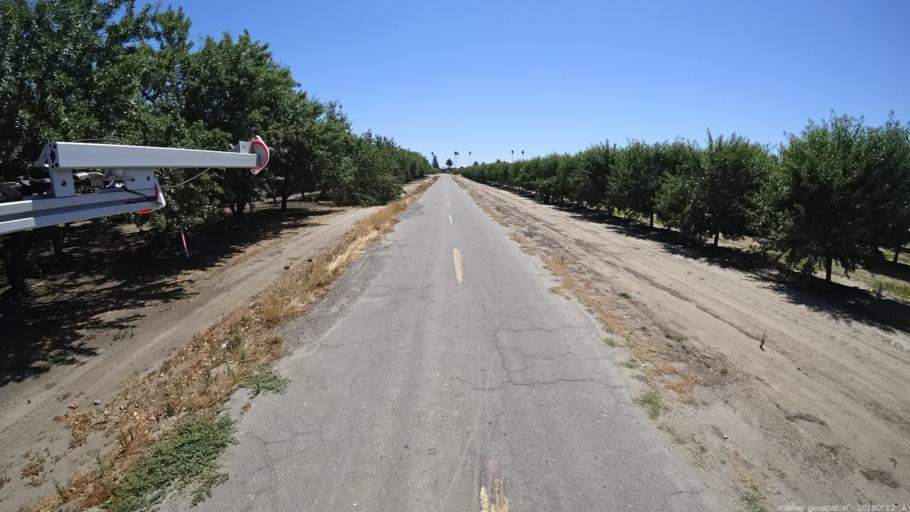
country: US
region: California
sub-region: Madera County
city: Chowchilla
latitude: 37.0472
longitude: -120.3325
